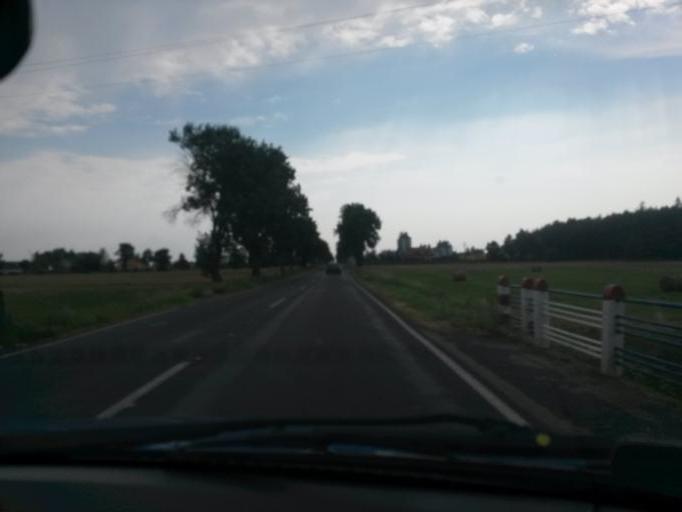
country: PL
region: Masovian Voivodeship
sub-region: Powiat zurominski
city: Biezun
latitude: 52.9969
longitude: 19.9183
